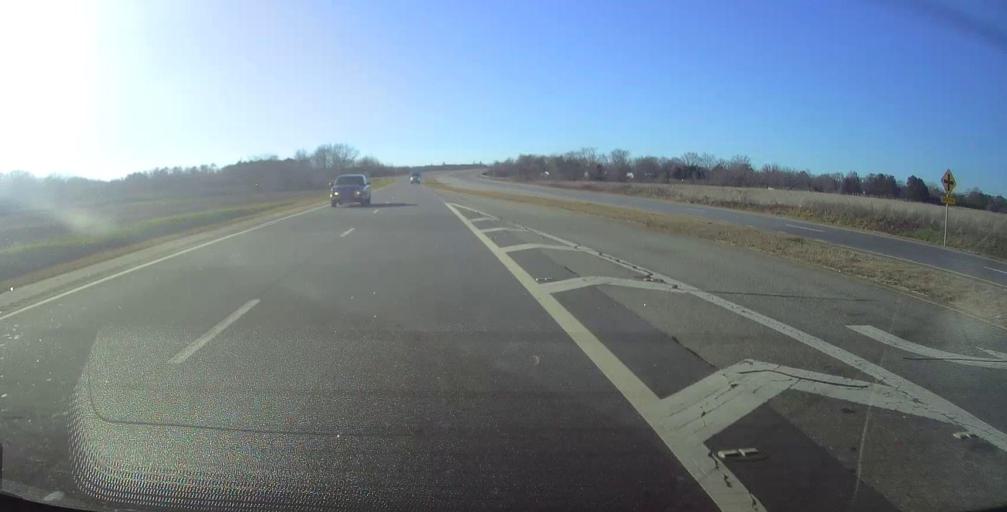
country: US
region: Georgia
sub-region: Lee County
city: Leesburg
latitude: 31.8918
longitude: -84.2525
